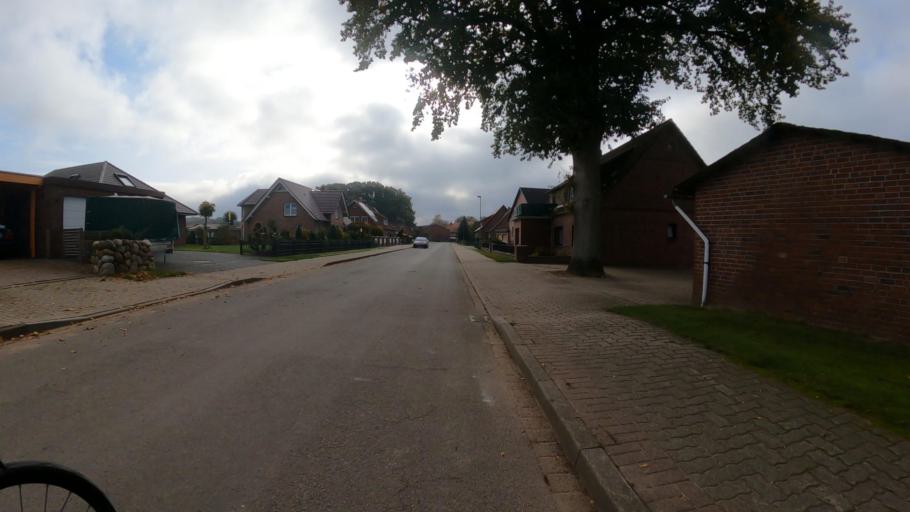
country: DE
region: Lower Saxony
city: Neu Wulmstorf
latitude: 53.4246
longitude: 9.8002
